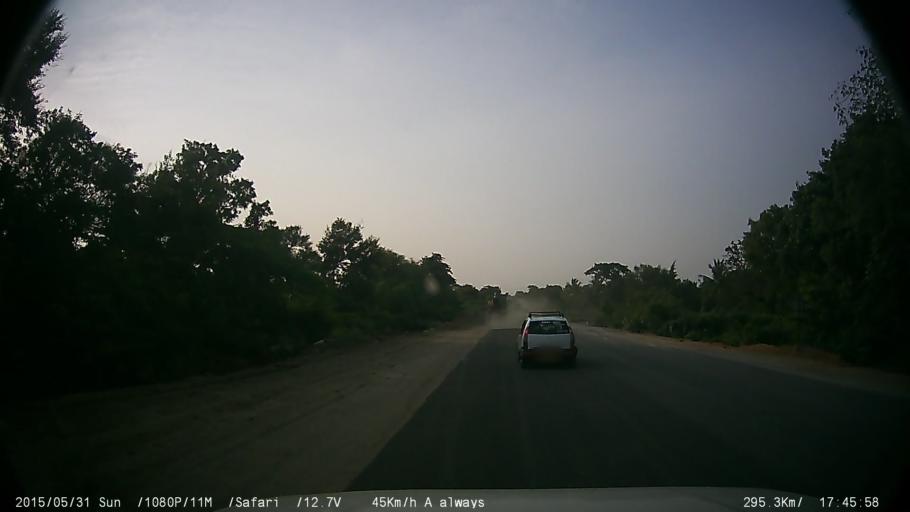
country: IN
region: Karnataka
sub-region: Chamrajnagar
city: Gundlupet
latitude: 11.9553
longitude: 76.6705
